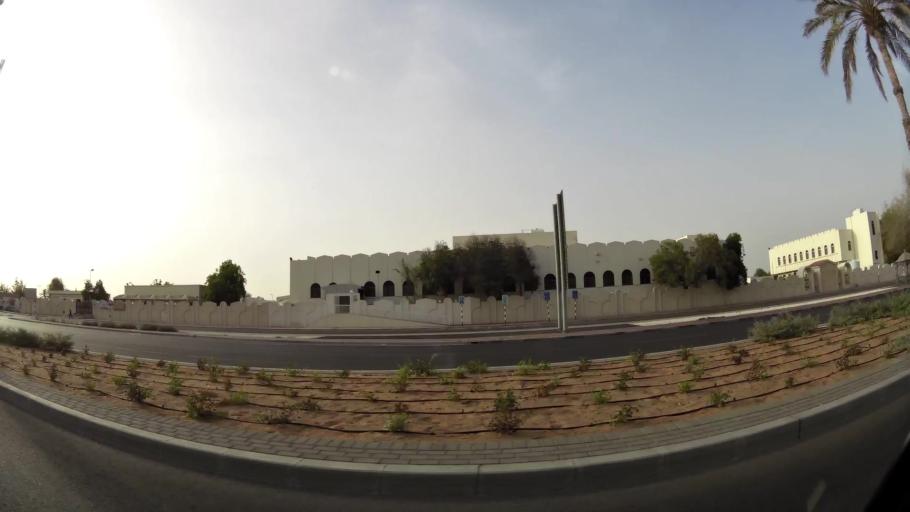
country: AE
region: Abu Dhabi
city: Al Ain
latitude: 24.2415
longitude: 55.7372
